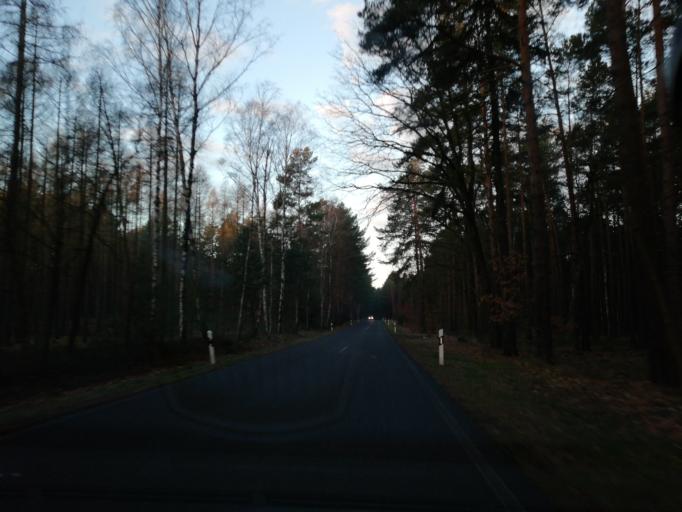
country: DE
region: Brandenburg
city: Bronkow
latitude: 51.7248
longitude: 13.8936
